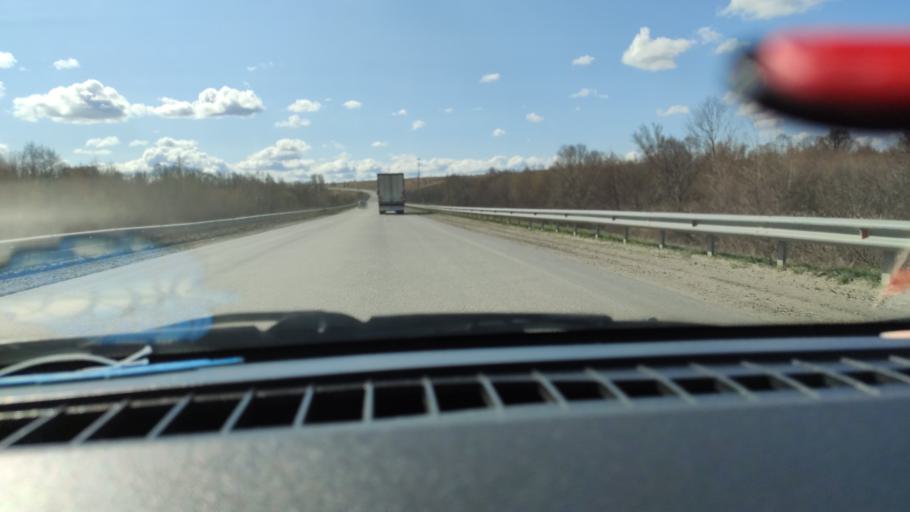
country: RU
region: Samara
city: Varlamovo
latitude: 53.1295
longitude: 48.2882
